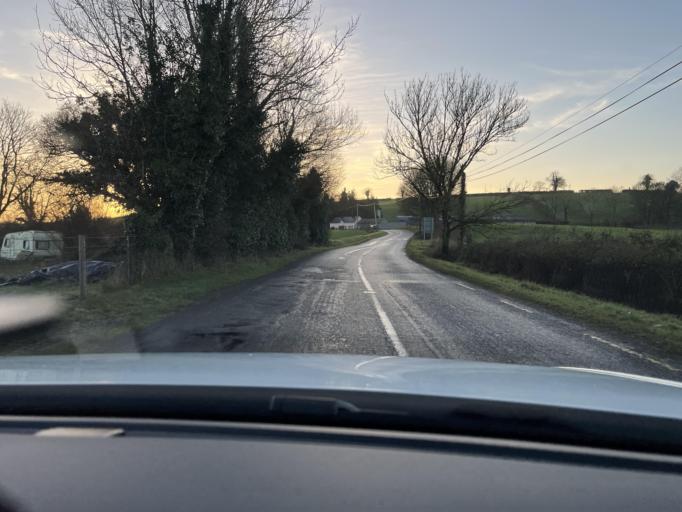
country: IE
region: Ulster
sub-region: An Cabhan
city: Ballyconnell
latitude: 54.0640
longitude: -7.6853
